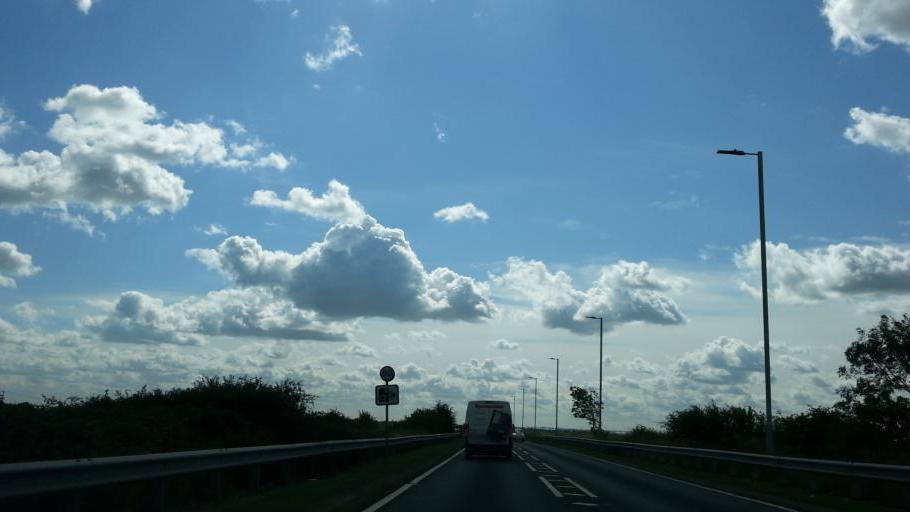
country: GB
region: England
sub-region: Essex
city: South Benfleet
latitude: 51.5497
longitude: 0.5414
